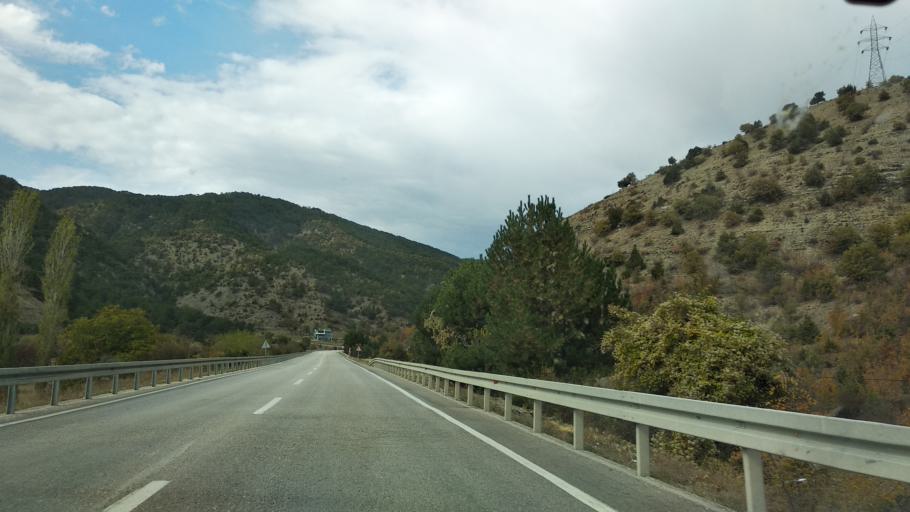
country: TR
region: Bolu
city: Mudurnu
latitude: 40.3385
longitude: 31.2456
